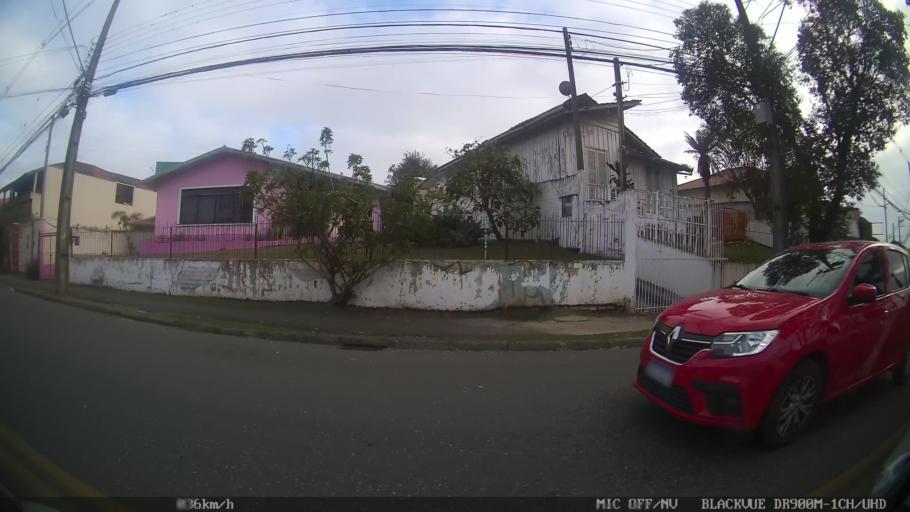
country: BR
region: Parana
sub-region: Curitiba
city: Curitiba
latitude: -25.4031
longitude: -49.3273
